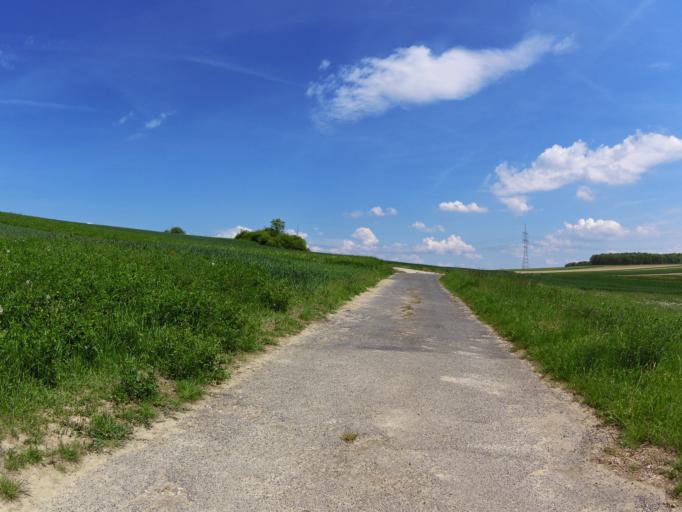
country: DE
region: Bavaria
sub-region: Regierungsbezirk Unterfranken
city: Theilheim
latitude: 49.7346
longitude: 10.0396
